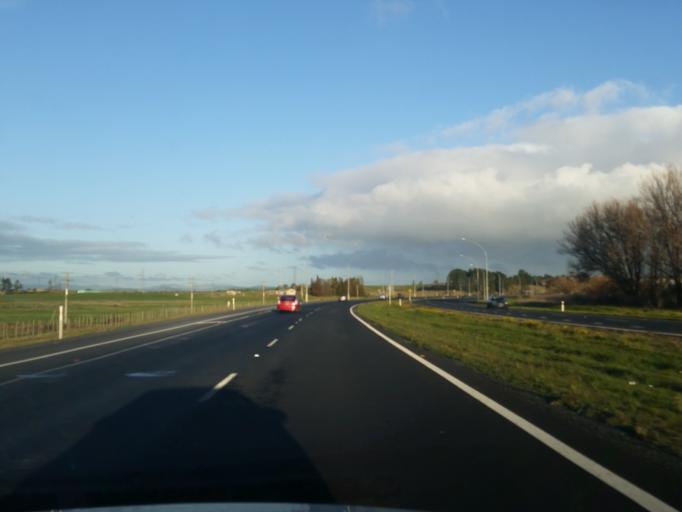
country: NZ
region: Waikato
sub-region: Waikato District
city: Te Kauwhata
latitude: -37.3046
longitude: 175.0645
